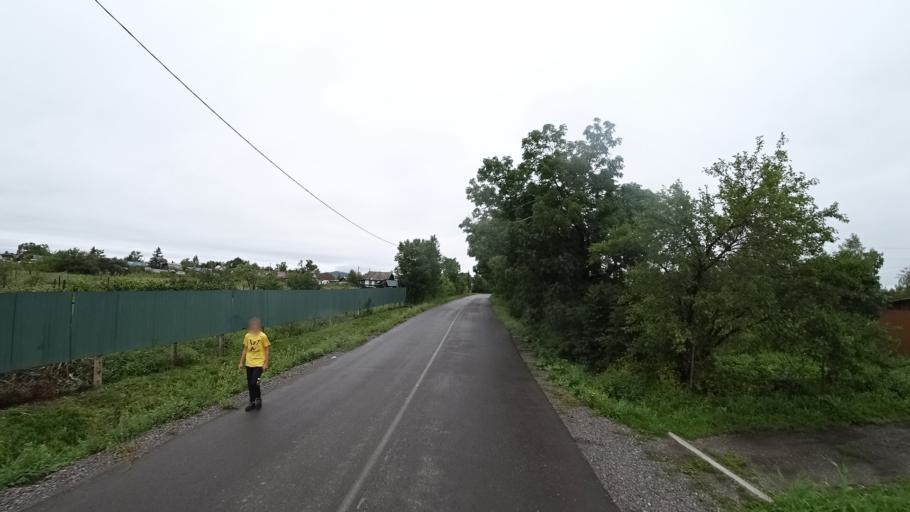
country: RU
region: Primorskiy
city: Monastyrishche
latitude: 44.2054
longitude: 132.4354
